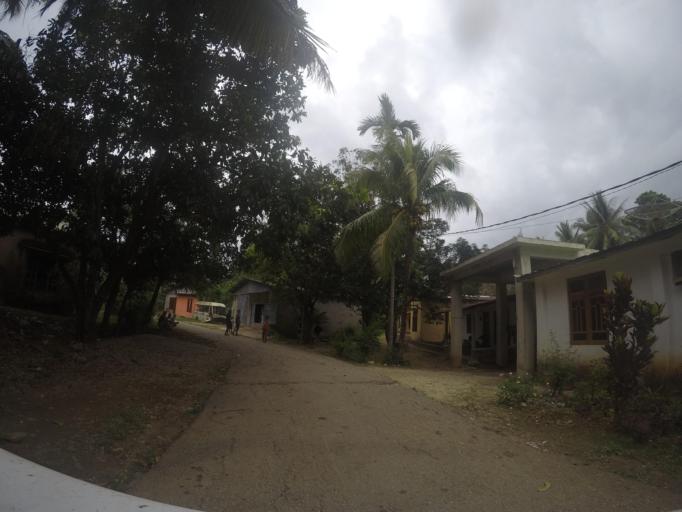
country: TL
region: Lautem
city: Lospalos
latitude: -8.5236
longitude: 126.9941
